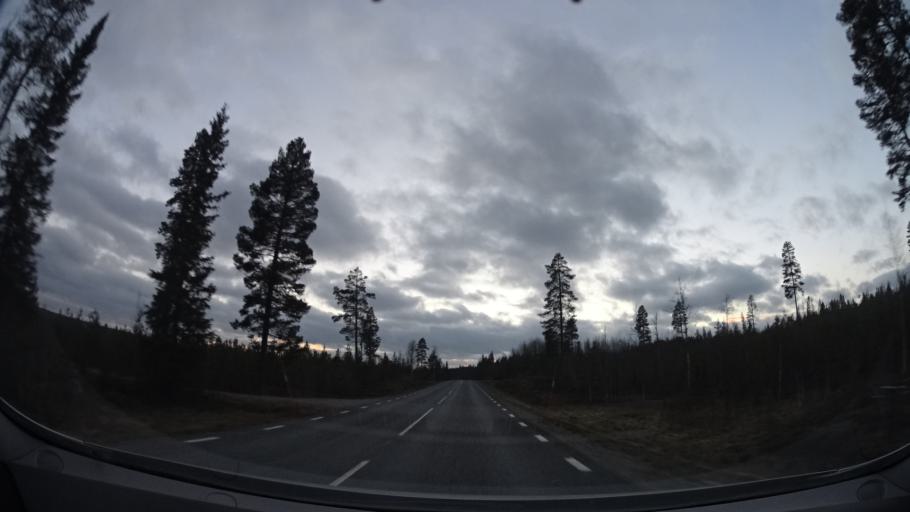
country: SE
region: Vaesterbotten
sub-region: Asele Kommun
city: Insjon
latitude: 64.3299
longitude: 17.7332
